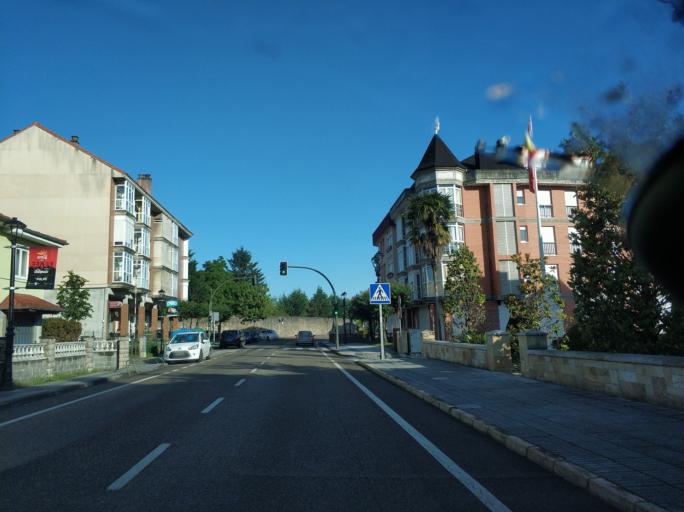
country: ES
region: Cantabria
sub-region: Provincia de Cantabria
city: Puente Viesgo
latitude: 43.3559
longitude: -3.9564
